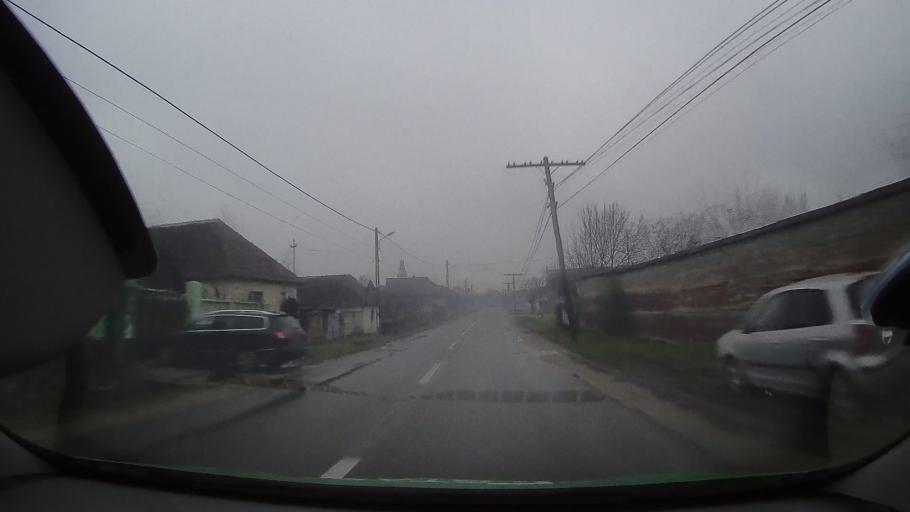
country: RO
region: Bihor
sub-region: Comuna Tinca
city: Gurbediu
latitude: 46.7928
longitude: 21.8639
